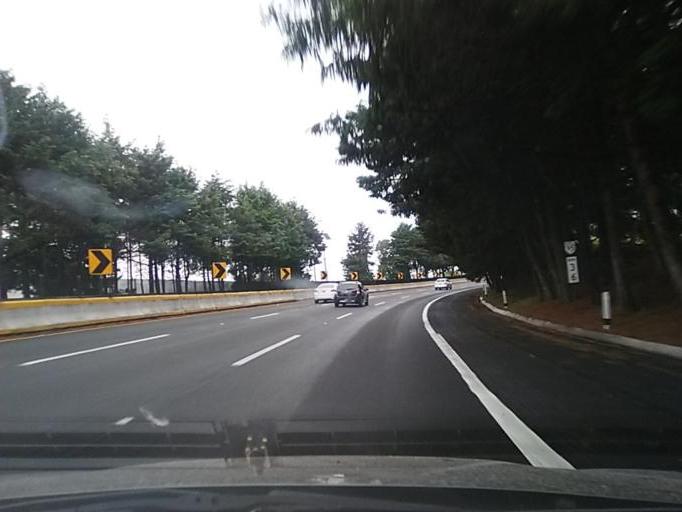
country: MX
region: Mexico City
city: Xochimilco
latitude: 19.1713
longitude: -99.1501
